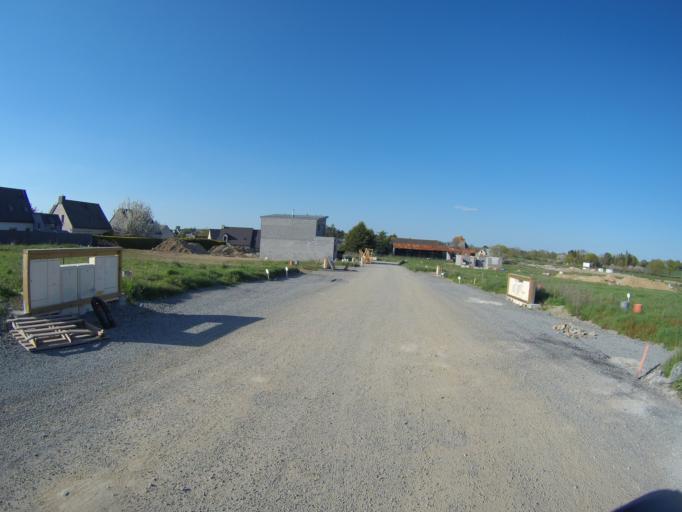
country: FR
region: Brittany
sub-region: Departement d'Ille-et-Vilaine
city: Vern-sur-Seiche
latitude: 48.0389
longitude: -1.5935
